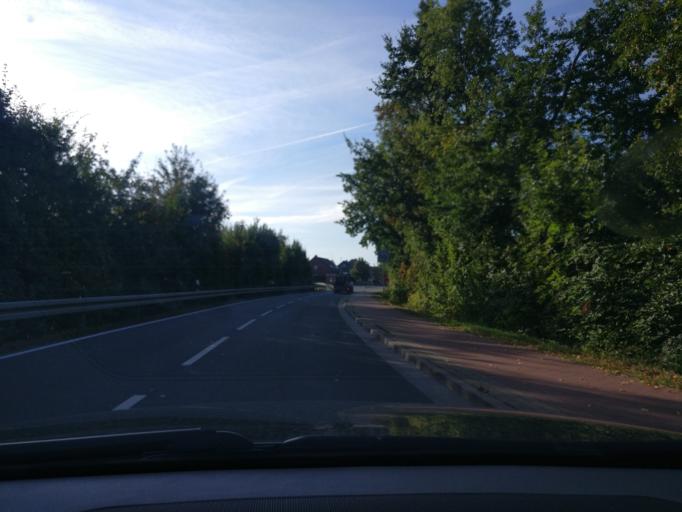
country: DE
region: Lower Saxony
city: Melle
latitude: 52.2120
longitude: 8.2767
